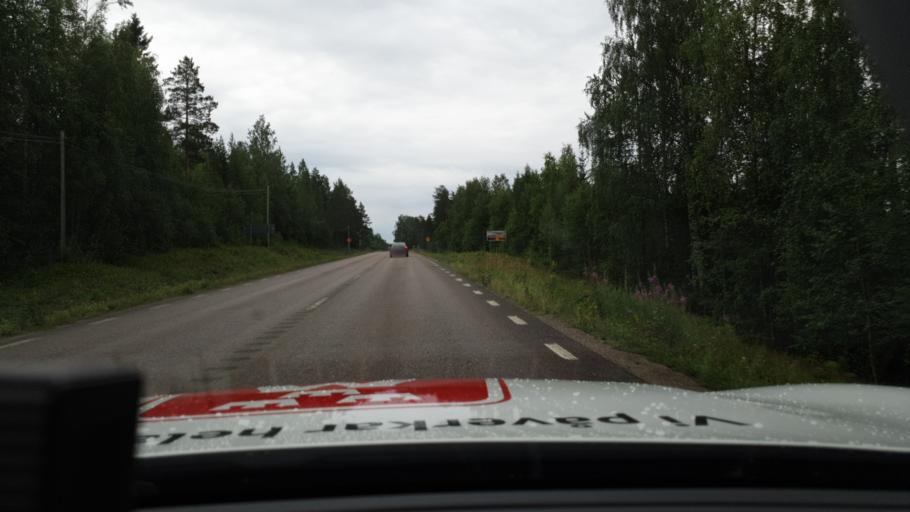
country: SE
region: Norrbotten
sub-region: Alvsbyns Kommun
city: AElvsbyn
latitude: 66.1132
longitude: 20.9287
